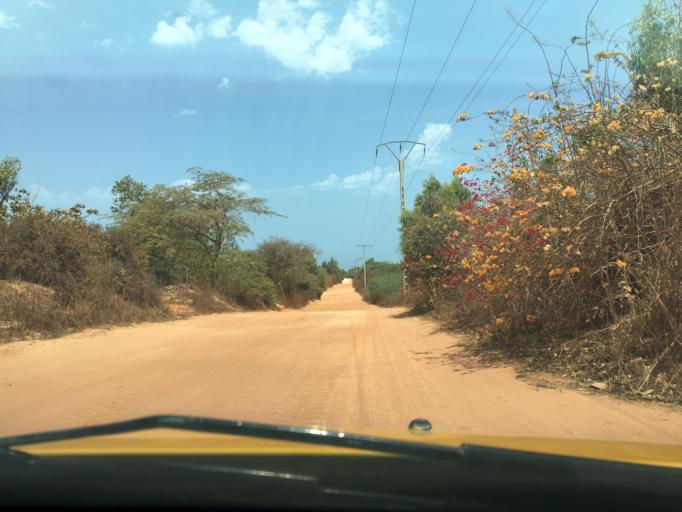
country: SN
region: Thies
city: Thies
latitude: 14.8184
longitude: -17.1989
